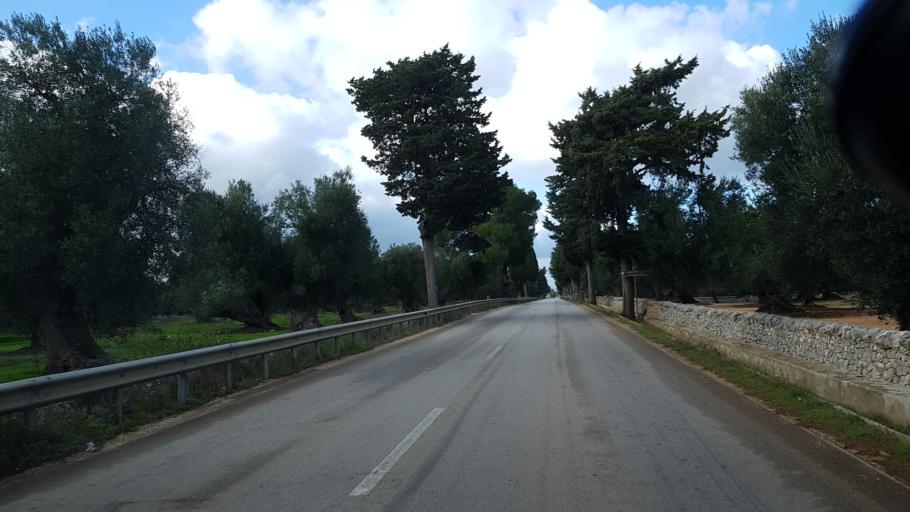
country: IT
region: Apulia
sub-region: Provincia di Brindisi
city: Montalbano
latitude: 40.7696
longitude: 17.5088
